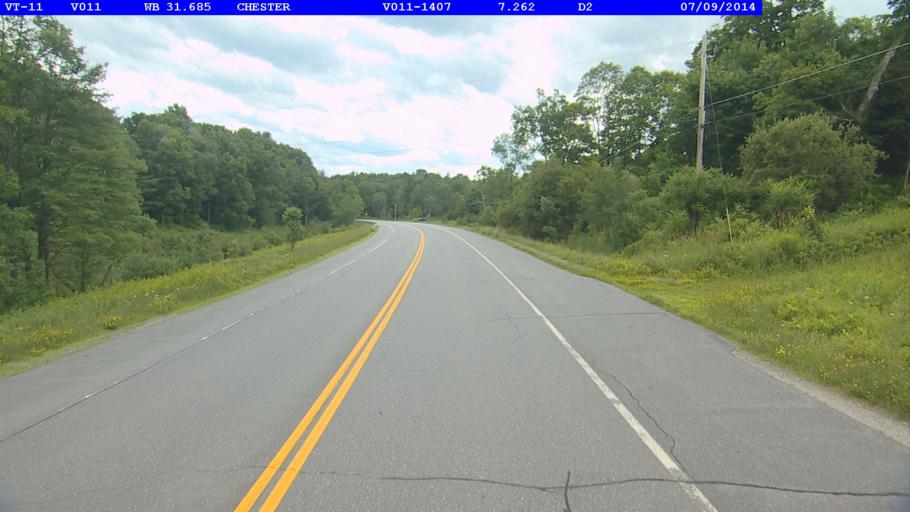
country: US
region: Vermont
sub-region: Windsor County
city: Chester
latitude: 43.2819
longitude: -72.5675
